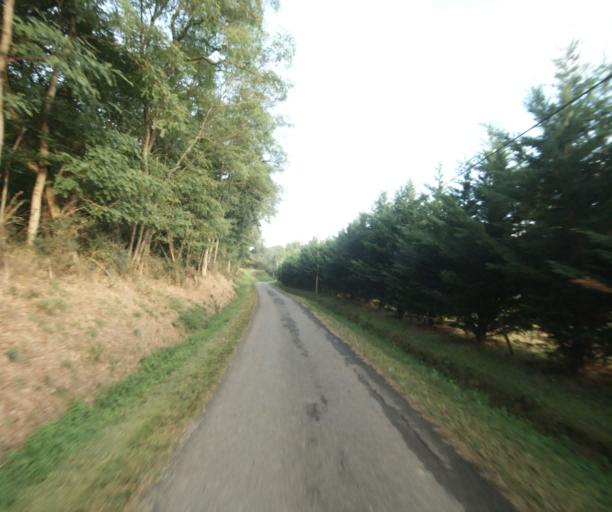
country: FR
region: Midi-Pyrenees
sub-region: Departement du Gers
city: Le Houga
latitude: 43.8417
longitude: -0.1103
